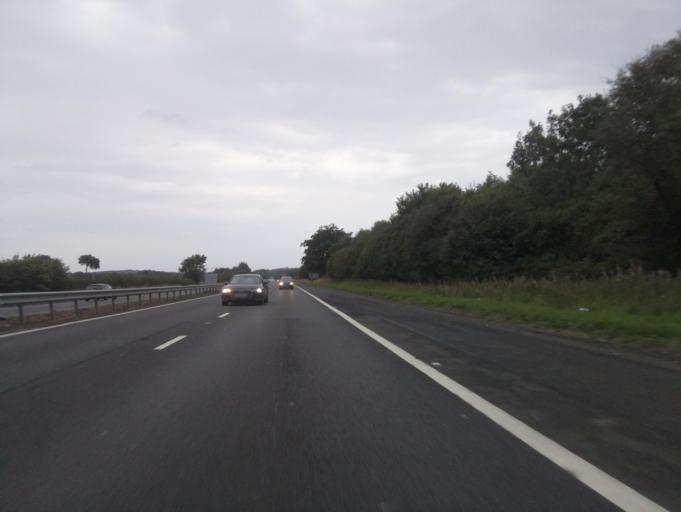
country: GB
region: Scotland
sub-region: North Lanarkshire
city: Harthill
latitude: 55.8693
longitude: -3.7270
